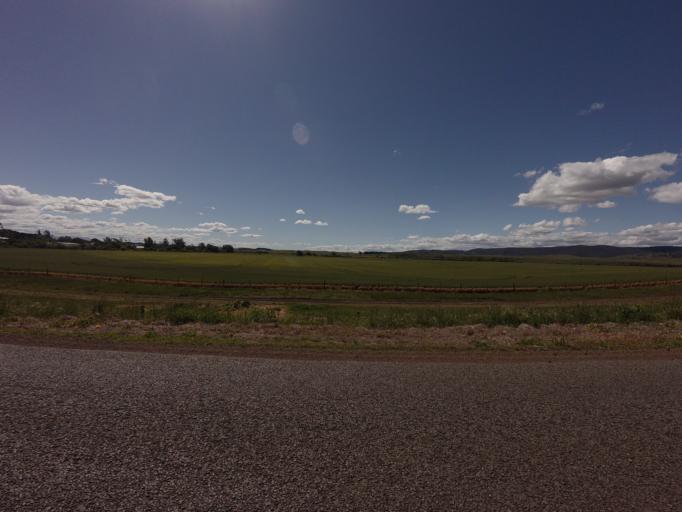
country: AU
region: Tasmania
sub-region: Northern Midlands
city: Evandale
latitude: -41.9410
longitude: 147.5415
